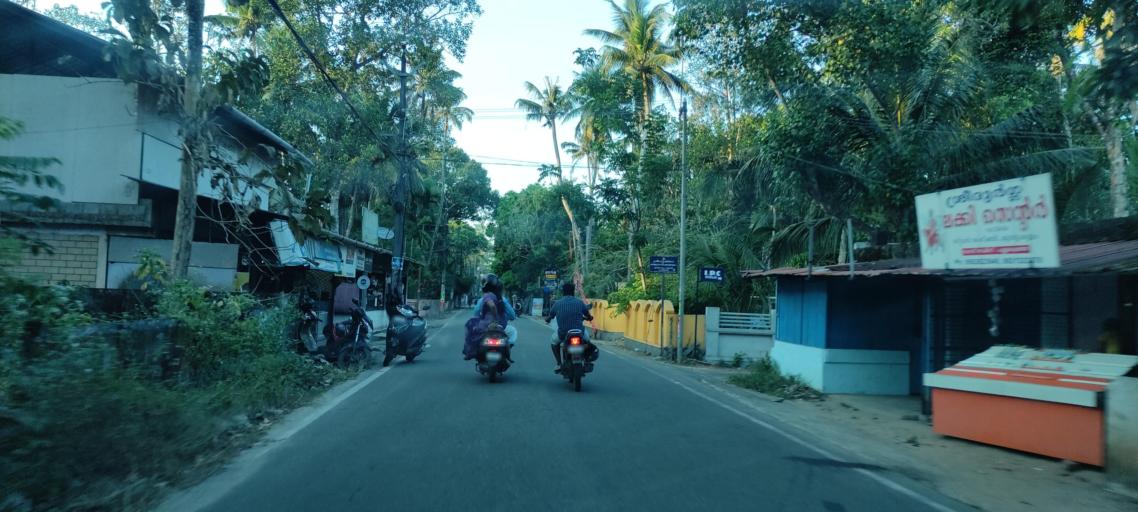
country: IN
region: Kerala
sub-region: Alappuzha
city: Kayankulam
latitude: 9.2201
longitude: 76.4607
